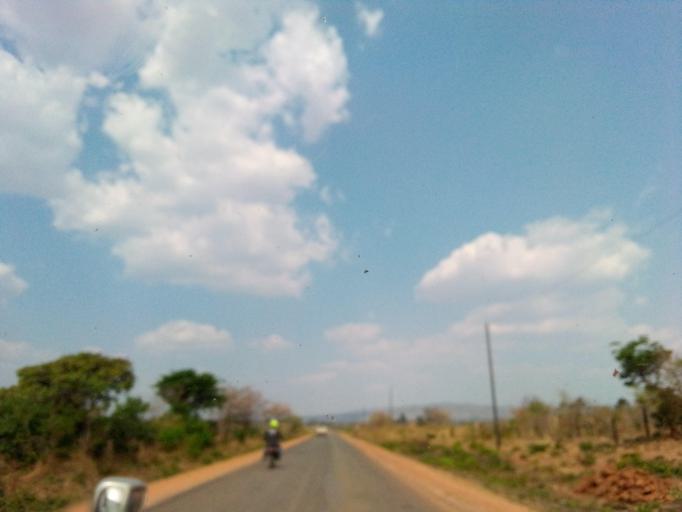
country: ZM
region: Northern
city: Mpika
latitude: -11.8332
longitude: 31.4131
